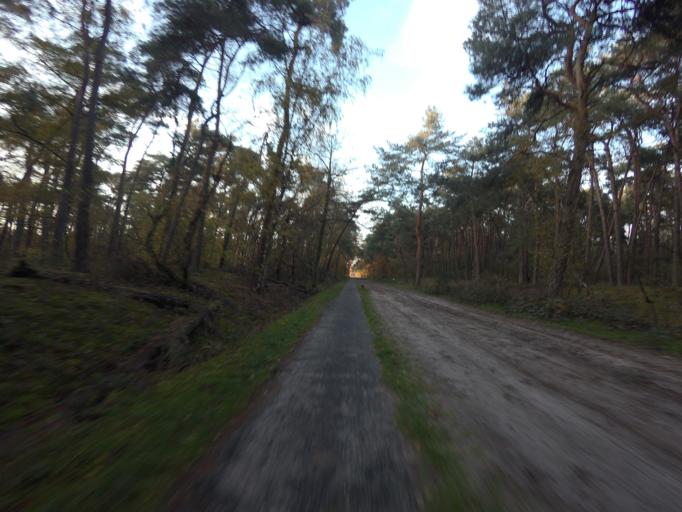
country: NL
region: North Brabant
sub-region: Gemeente Breda
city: Breda
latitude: 51.5169
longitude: 4.8133
